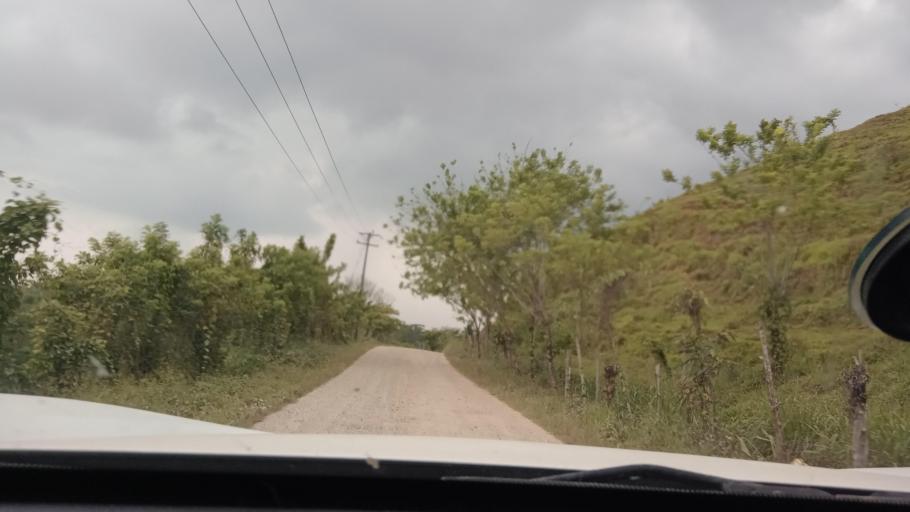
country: MX
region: Tabasco
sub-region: Huimanguillo
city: Francisco Rueda
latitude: 17.4379
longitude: -94.0591
